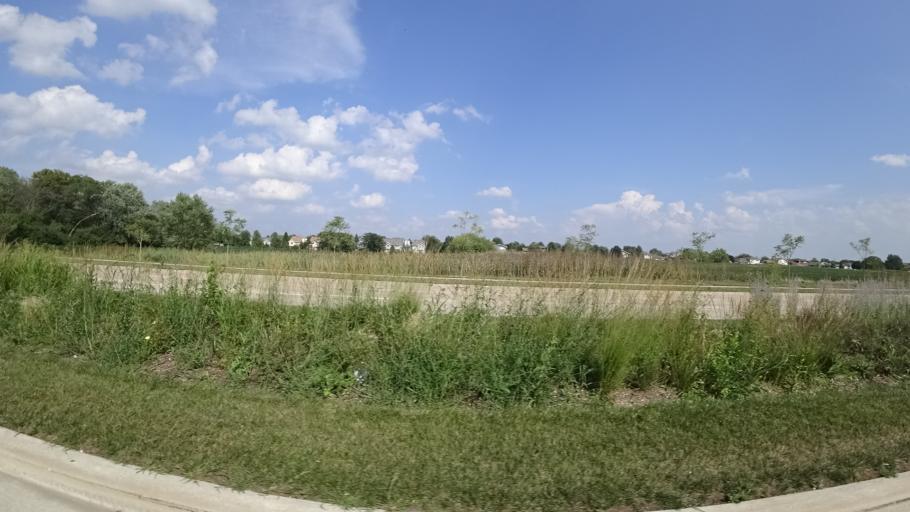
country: US
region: Illinois
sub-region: Cook County
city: Orland Hills
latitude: 41.5702
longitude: -87.8517
